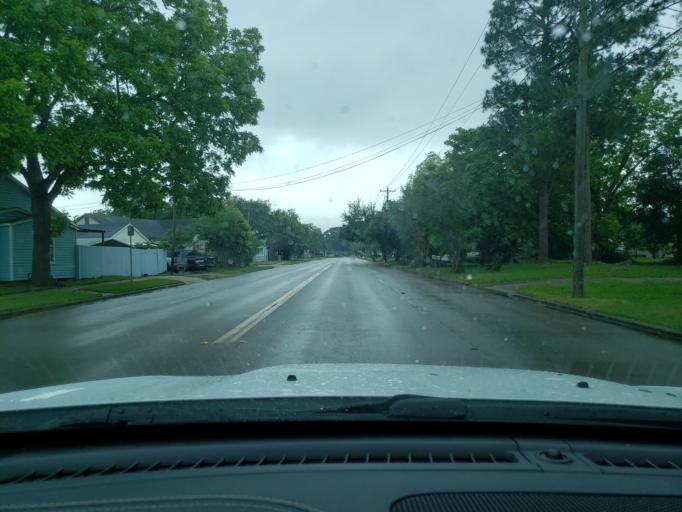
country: US
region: Texas
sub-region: Harris County
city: Baytown
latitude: 29.7417
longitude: -94.9714
